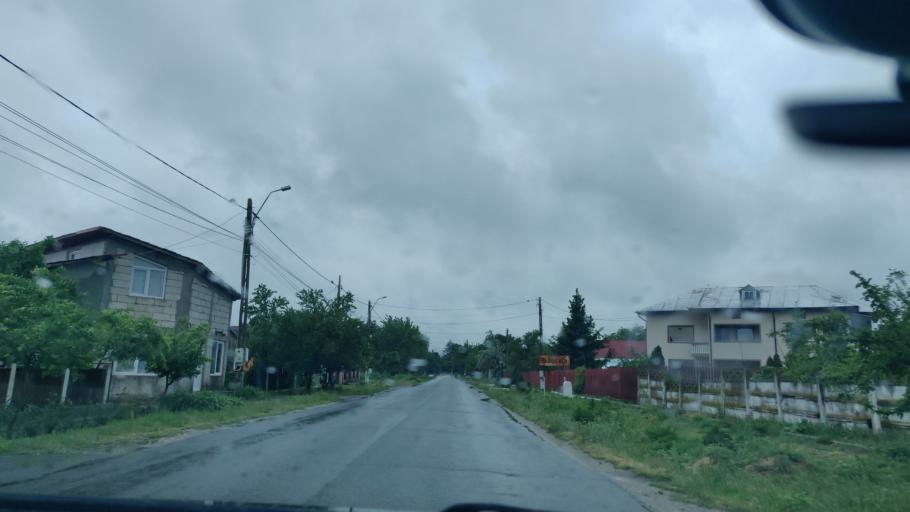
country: RO
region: Giurgiu
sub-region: Comuna Bulbucata
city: Bulbucata
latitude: 44.2735
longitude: 25.8293
